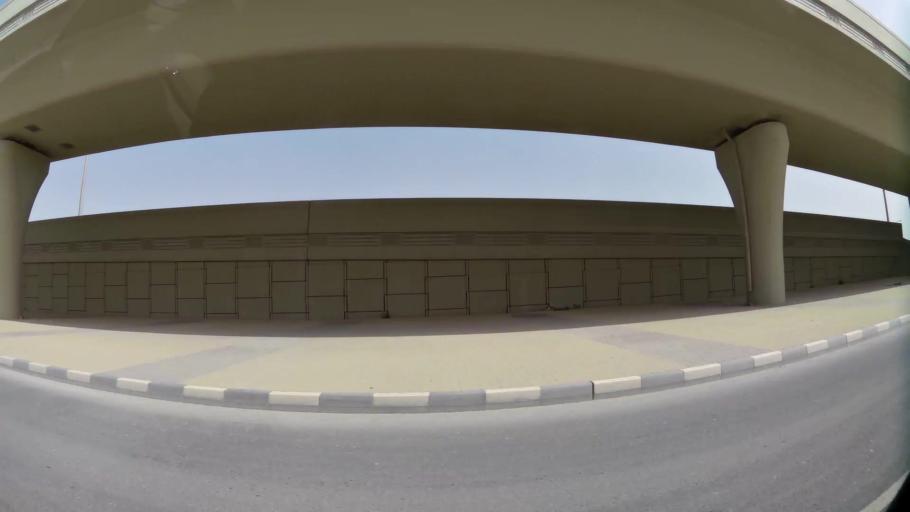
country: QA
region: Baladiyat ad Dawhah
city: Doha
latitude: 25.2948
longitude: 51.4775
